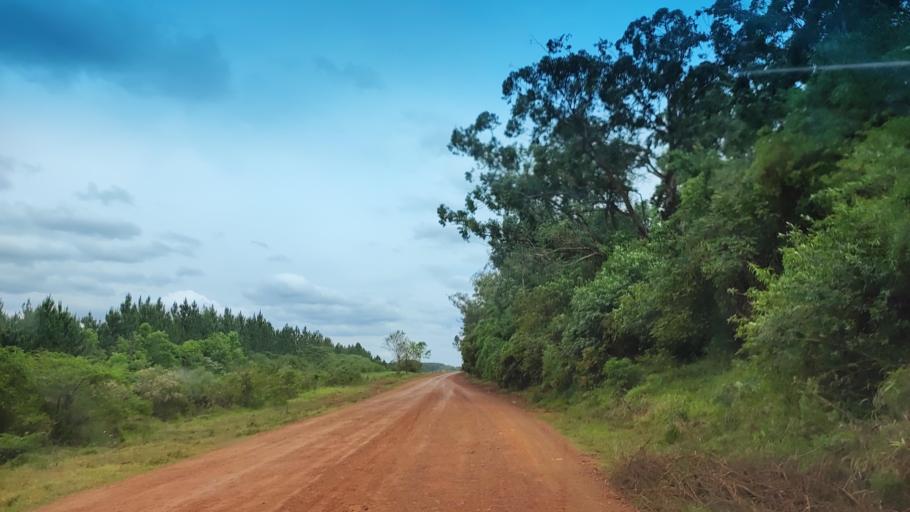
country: AR
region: Misiones
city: Garupa
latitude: -27.4921
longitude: -55.9709
